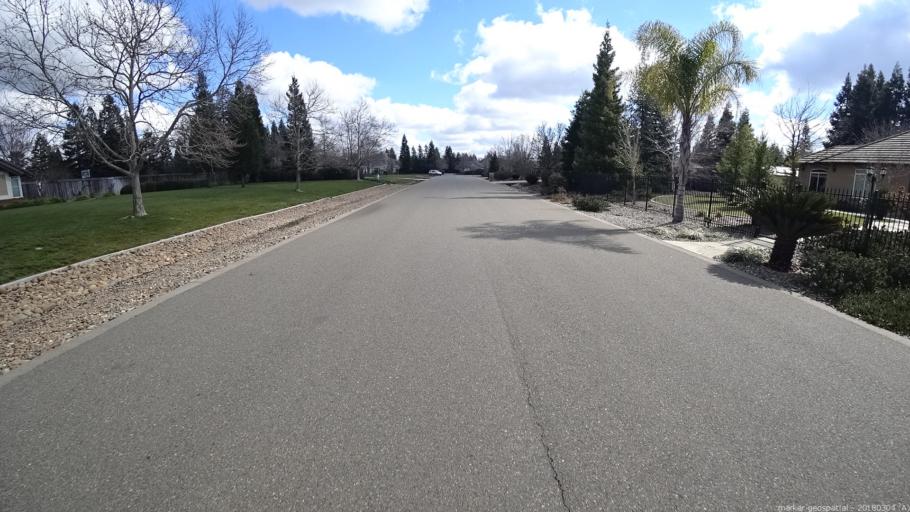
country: US
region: California
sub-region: Sacramento County
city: Vineyard
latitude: 38.4607
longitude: -121.3087
